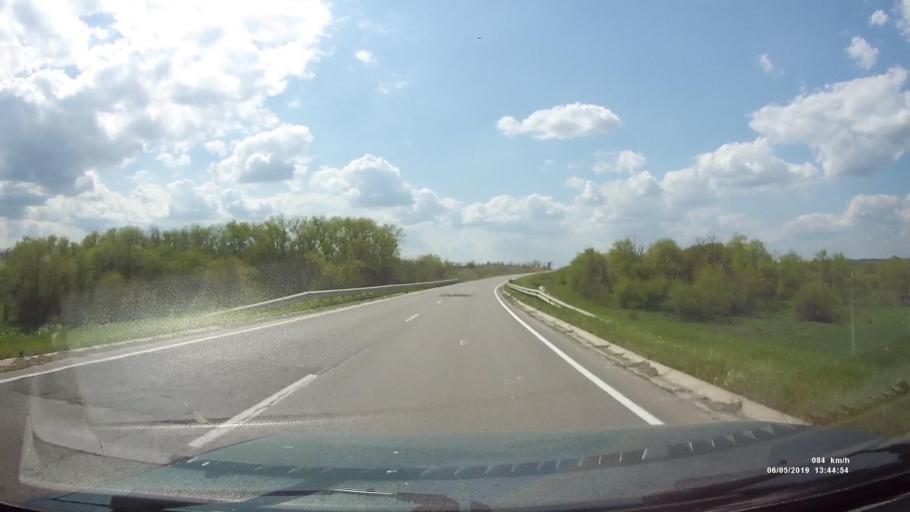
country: RU
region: Rostov
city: Melikhovskaya
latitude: 47.6571
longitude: 40.6110
